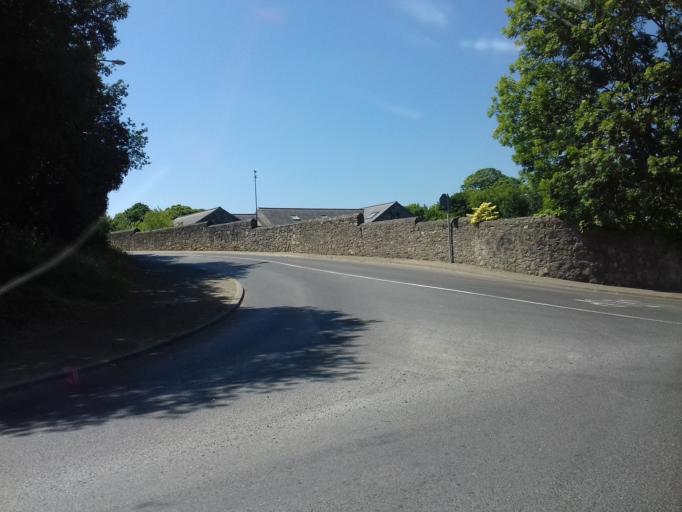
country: IE
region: Leinster
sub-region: An Mhi
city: Stamullin
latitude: 53.5874
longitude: -6.2917
